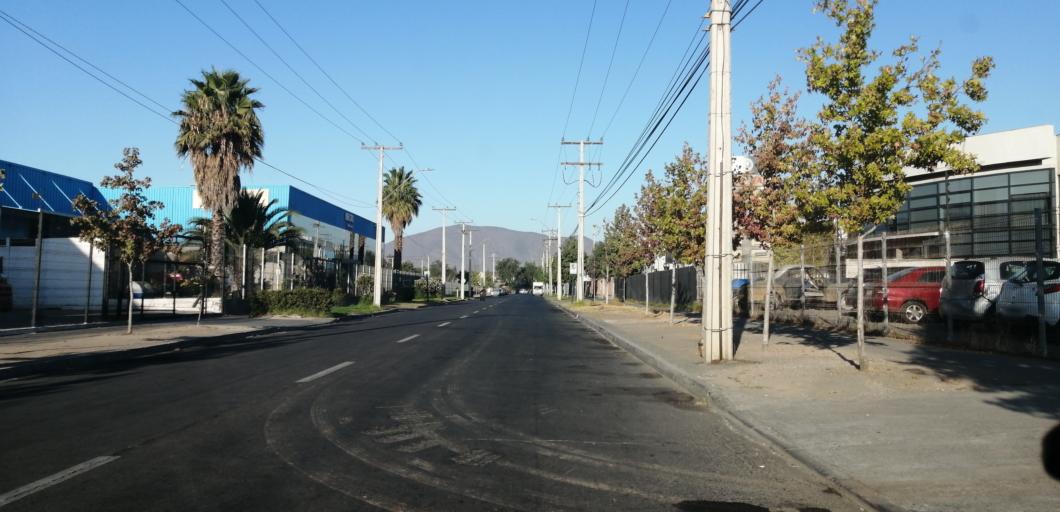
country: CL
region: Santiago Metropolitan
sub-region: Provincia de Santiago
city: Lo Prado
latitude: -33.4322
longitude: -70.7762
